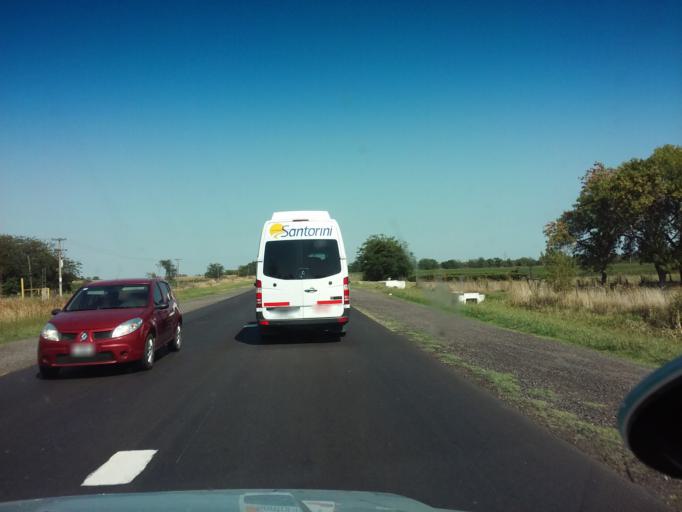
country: AR
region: Buenos Aires
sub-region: Partido de Chivilcoy
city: Chivilcoy
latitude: -34.9602
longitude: -60.0425
